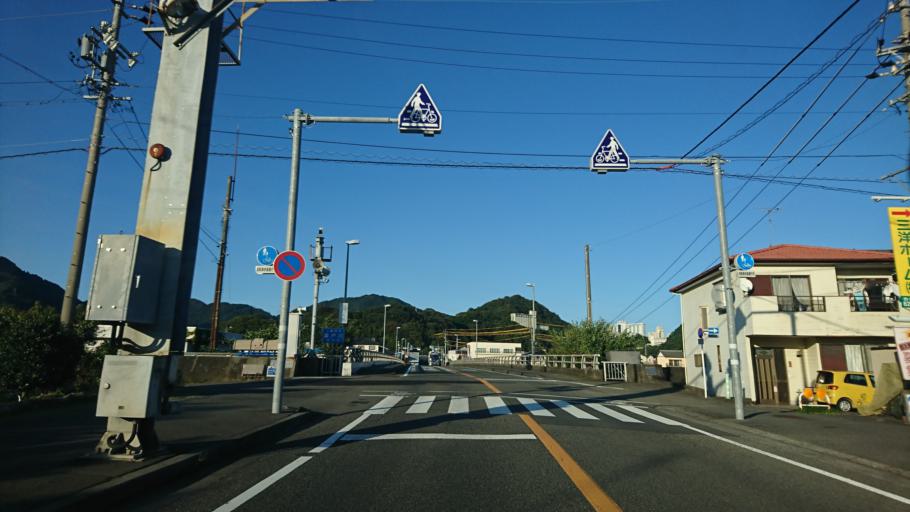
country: JP
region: Shizuoka
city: Yaizu
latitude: 34.8762
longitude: 138.3265
